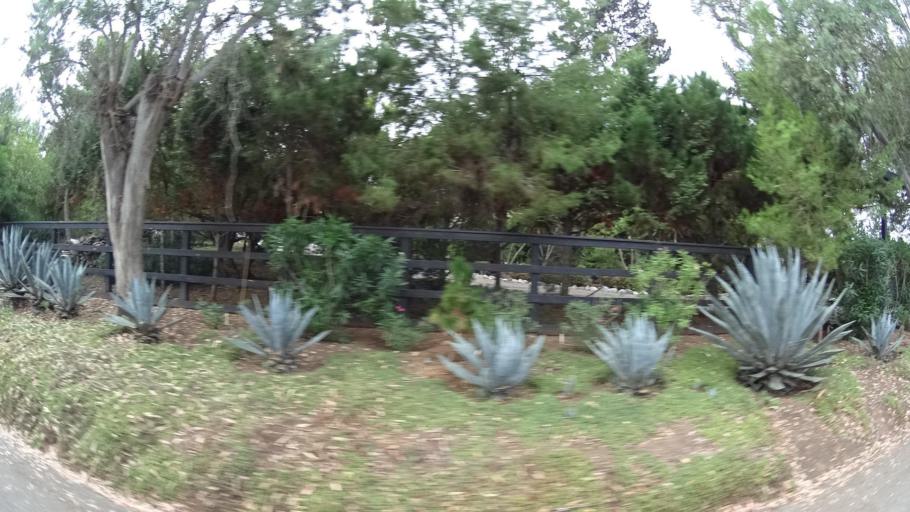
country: US
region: California
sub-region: San Diego County
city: Solana Beach
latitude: 32.9956
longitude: -117.2367
